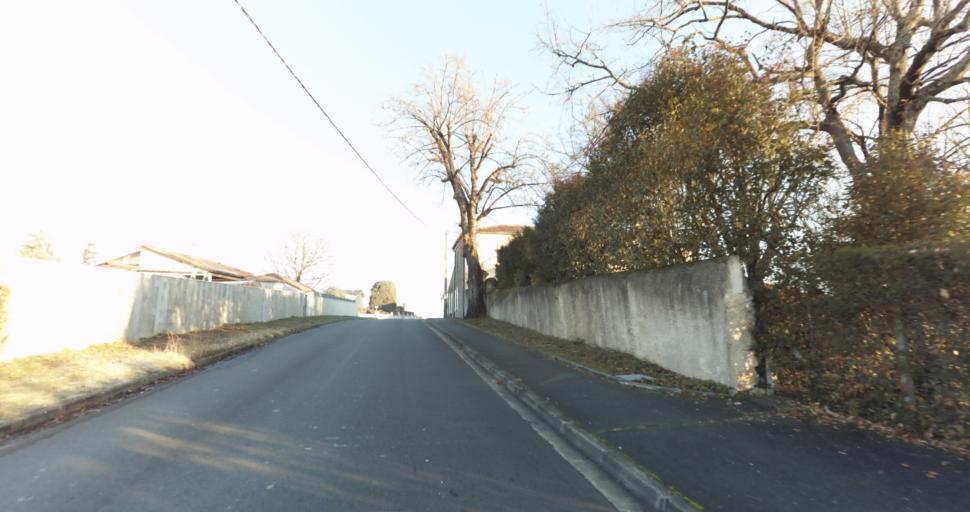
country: FR
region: Aquitaine
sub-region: Departement de la Gironde
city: Carbon-Blanc
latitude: 44.9091
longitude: -0.5029
